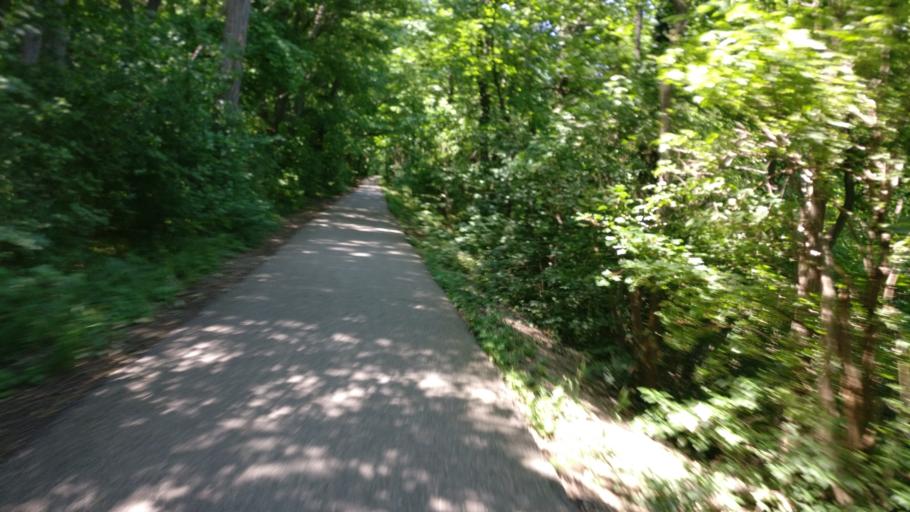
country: AT
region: Lower Austria
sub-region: Politischer Bezirk Baden
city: Teesdorf
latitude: 47.9489
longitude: 16.2738
